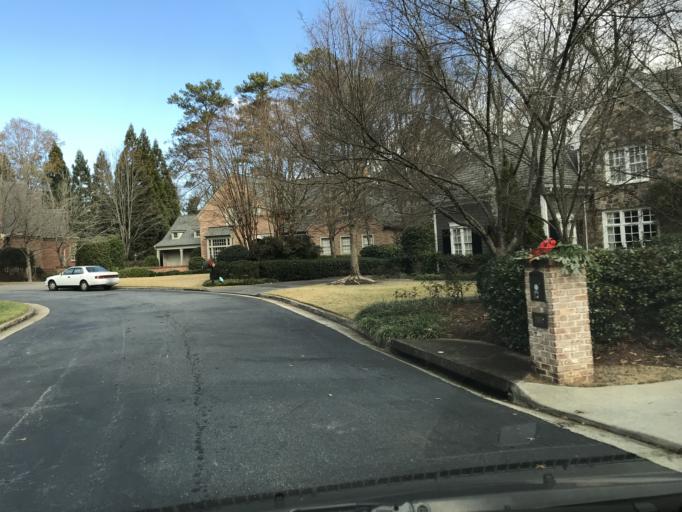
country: US
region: Georgia
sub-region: DeKalb County
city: North Atlanta
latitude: 33.8727
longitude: -84.3450
